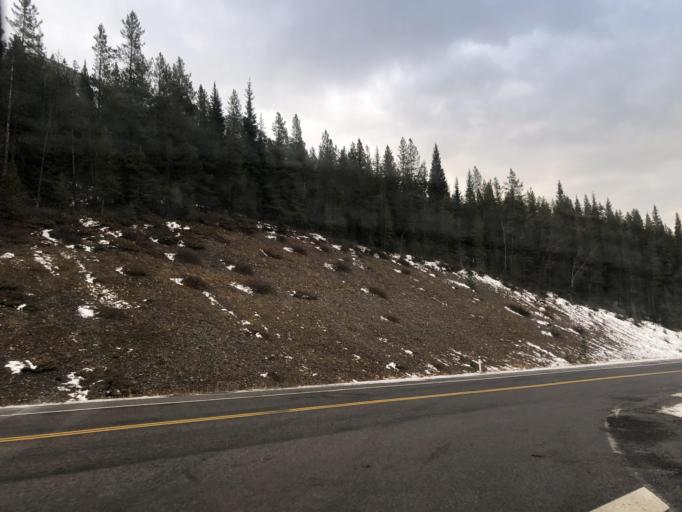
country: CA
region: Alberta
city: Canmore
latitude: 50.7065
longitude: -115.1112
